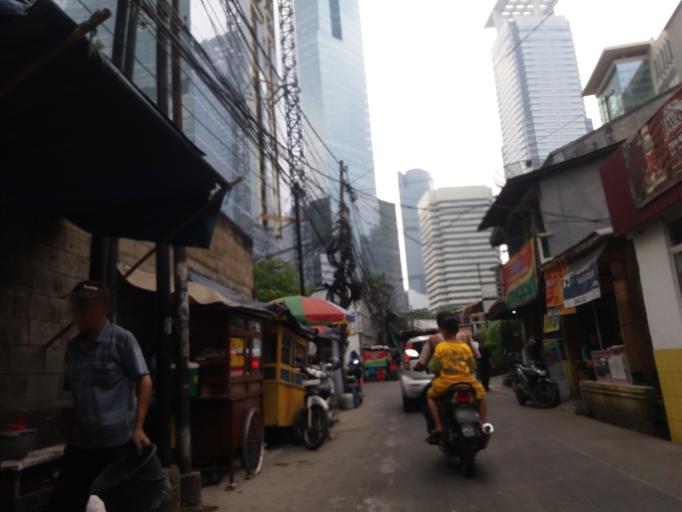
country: ID
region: Jakarta Raya
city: Jakarta
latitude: -6.2138
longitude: 106.8217
